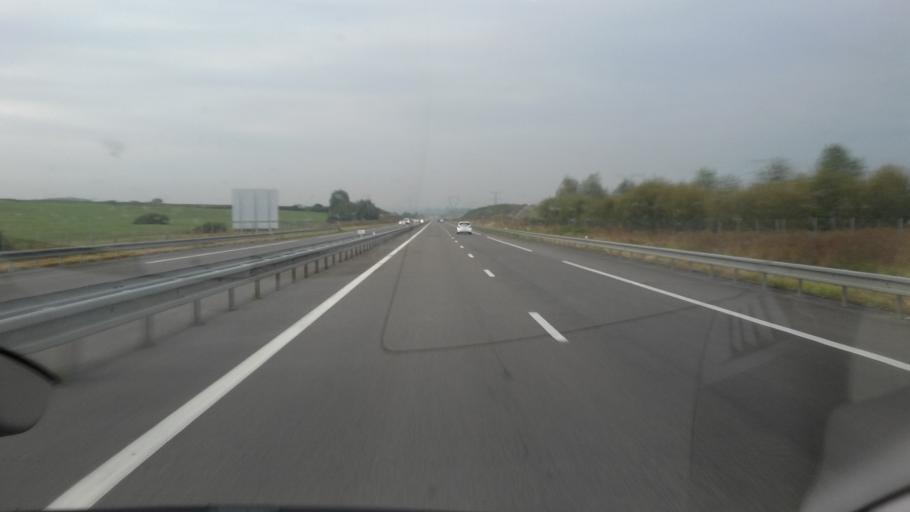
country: FR
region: Champagne-Ardenne
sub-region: Departement des Ardennes
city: Rethel
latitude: 49.5789
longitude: 4.4826
